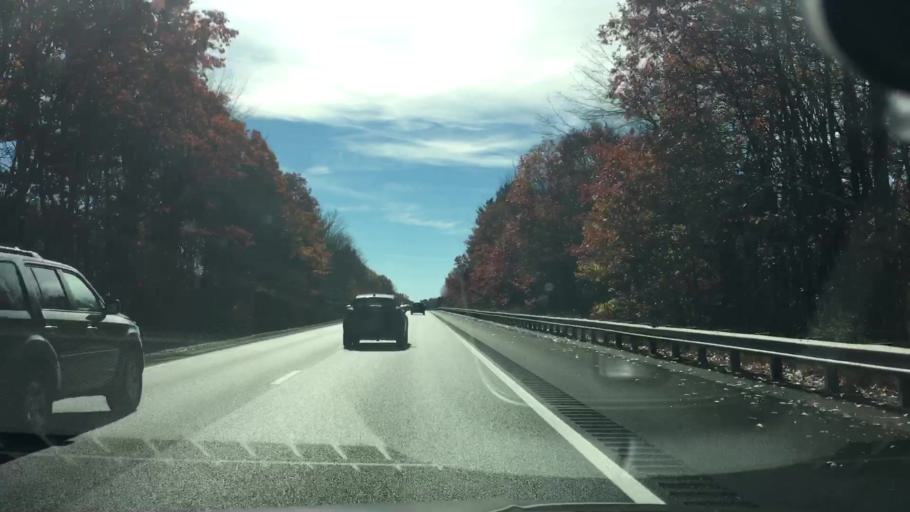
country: US
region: Massachusetts
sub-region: Franklin County
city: Whately
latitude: 42.4412
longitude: -72.6208
